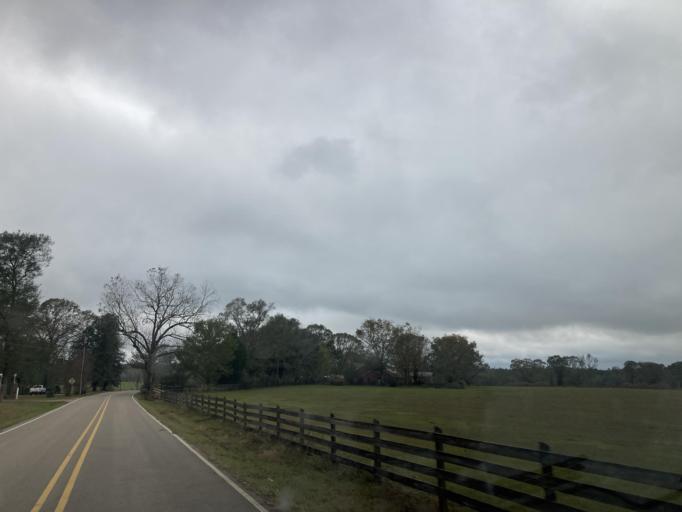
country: US
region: Mississippi
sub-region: Lamar County
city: Purvis
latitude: 31.1822
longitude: -89.4561
